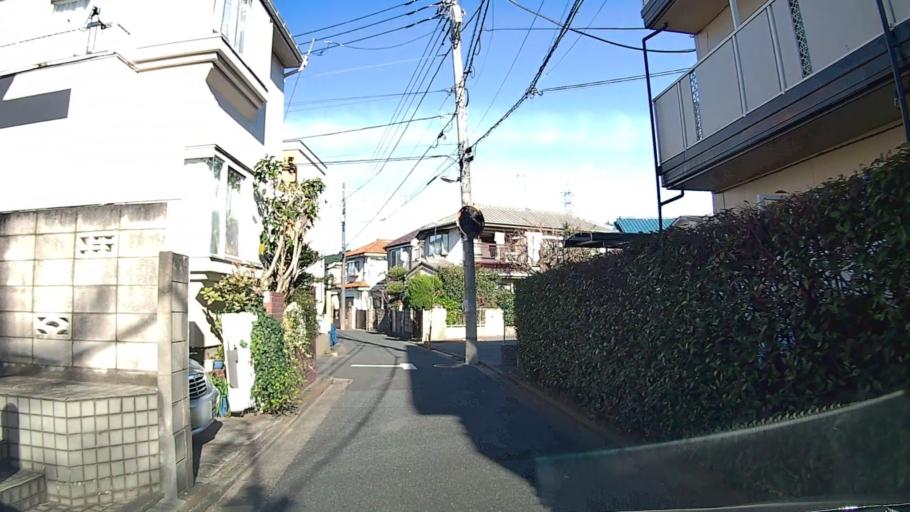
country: JP
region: Saitama
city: Wako
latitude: 35.7580
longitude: 139.6124
